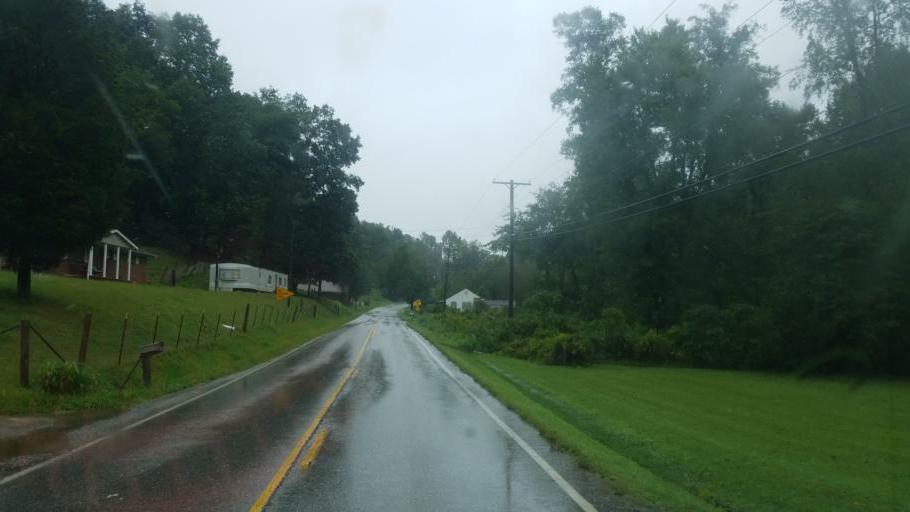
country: US
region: Kentucky
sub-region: Greenup County
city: South Shore
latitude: 38.7102
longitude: -82.9509
